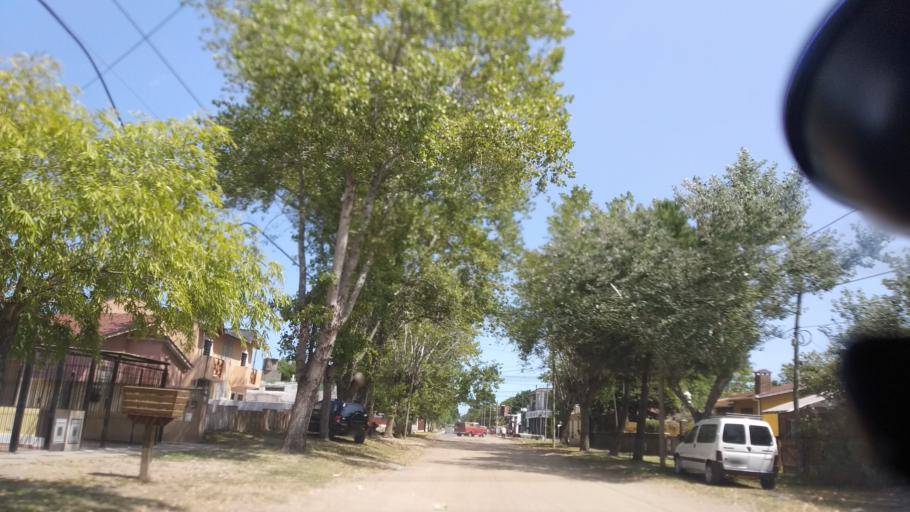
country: AR
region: Buenos Aires
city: Mar del Tuyu
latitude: -36.5692
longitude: -56.6941
